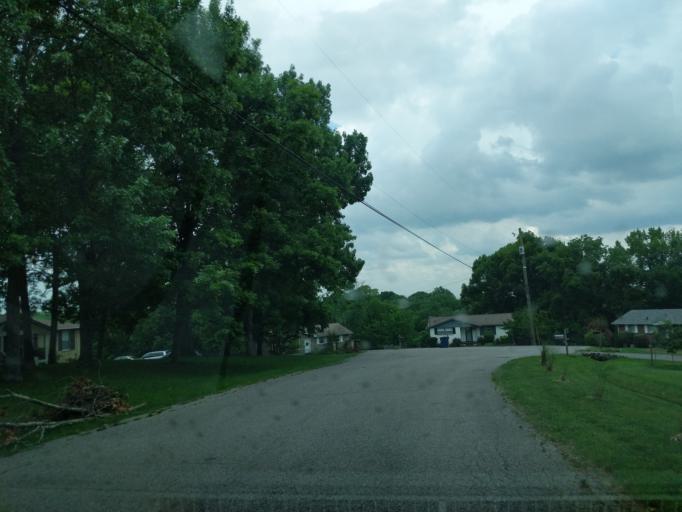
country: US
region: Tennessee
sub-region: Davidson County
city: Goodlettsville
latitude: 36.3138
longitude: -86.7248
